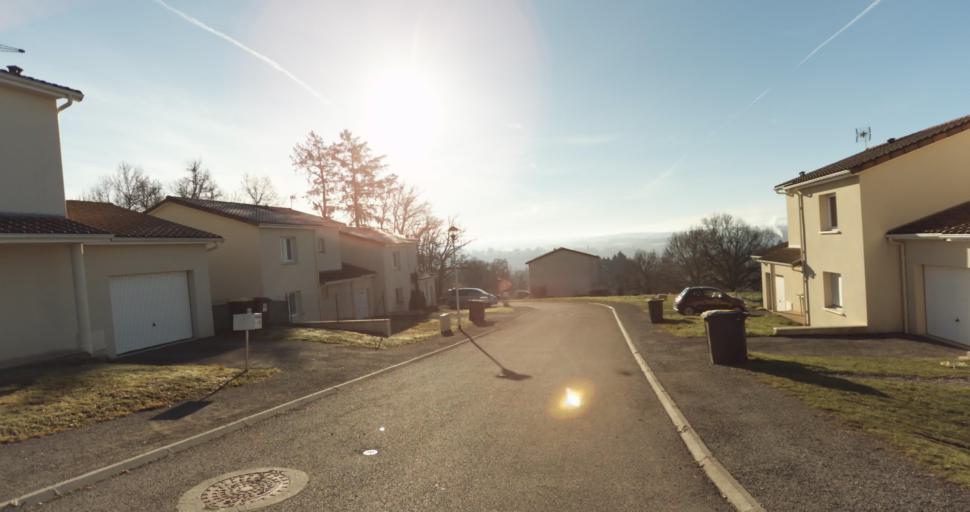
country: FR
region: Limousin
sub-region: Departement de la Haute-Vienne
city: Aixe-sur-Vienne
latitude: 45.8081
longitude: 1.1531
